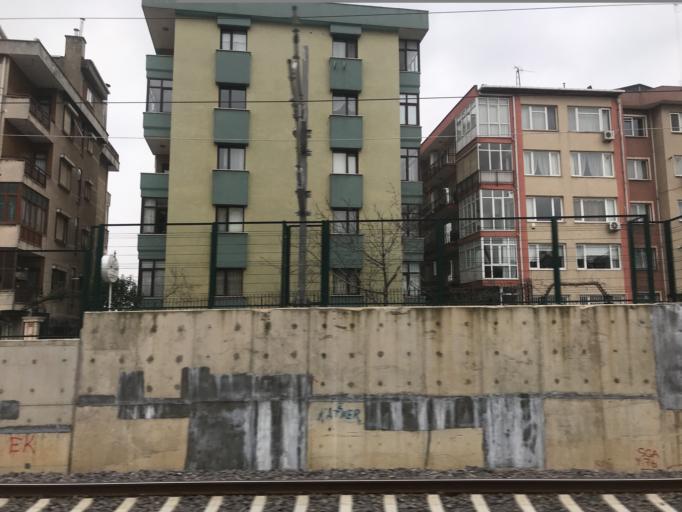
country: TR
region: Istanbul
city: Adalar
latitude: 40.8874
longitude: 29.1809
